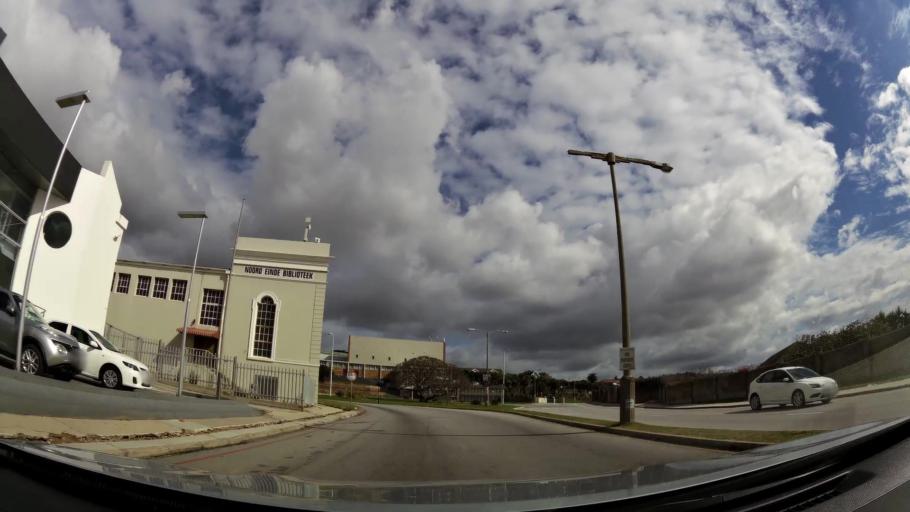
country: ZA
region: Eastern Cape
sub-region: Nelson Mandela Bay Metropolitan Municipality
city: Port Elizabeth
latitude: -33.9471
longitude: 25.6036
